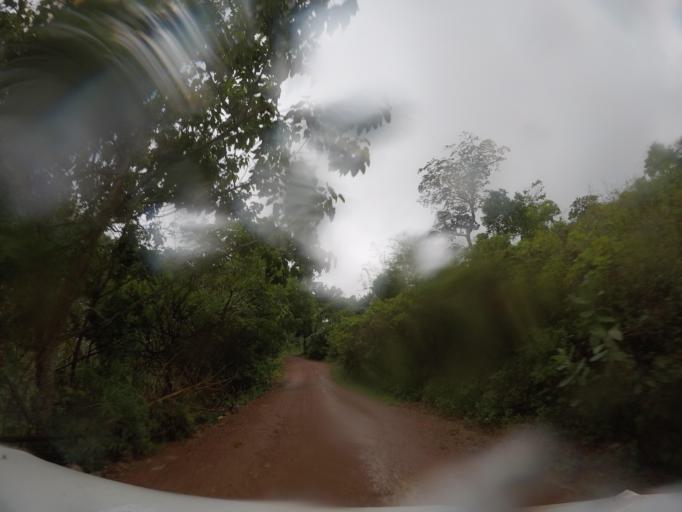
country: TL
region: Baucau
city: Venilale
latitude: -8.6306
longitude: 126.4292
